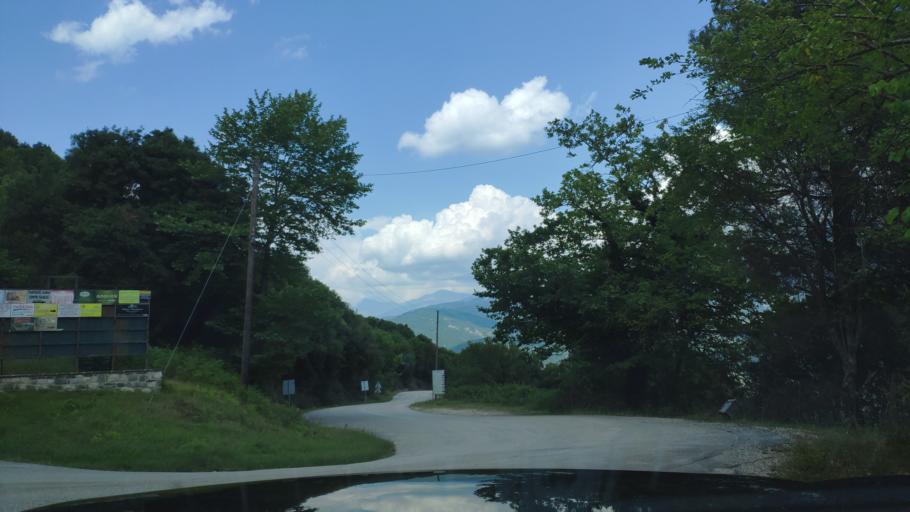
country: GR
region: Epirus
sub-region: Nomos Artas
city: Agios Dimitrios
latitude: 39.4532
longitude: 21.0216
